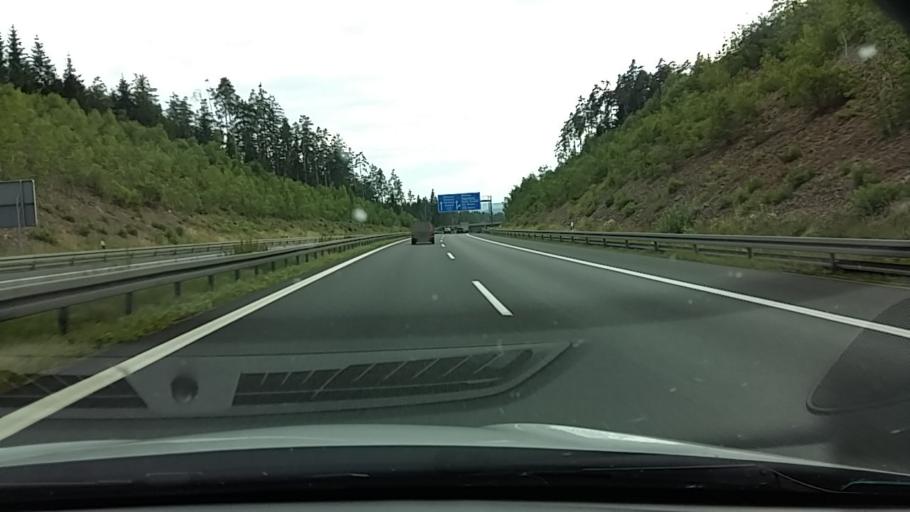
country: DE
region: Bavaria
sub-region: Upper Palatinate
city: Wernberg-Koblitz
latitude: 49.5291
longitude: 12.1855
